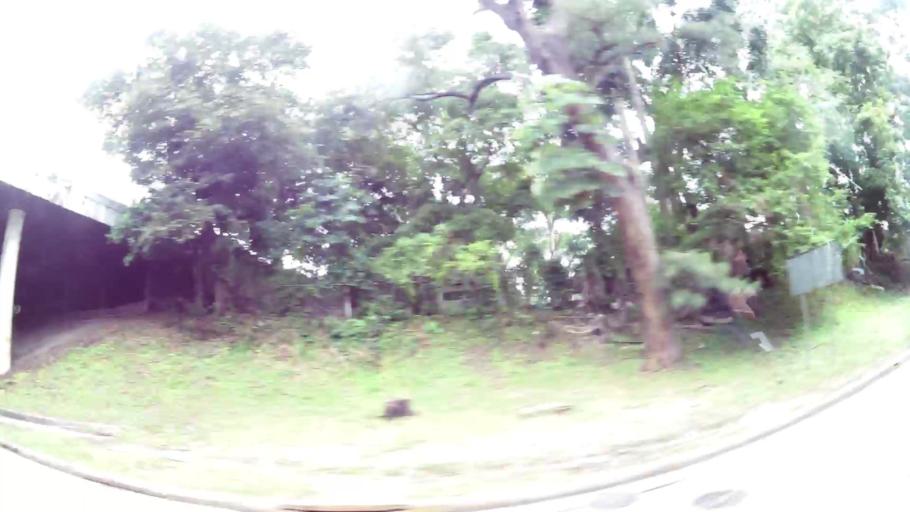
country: PA
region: Panama
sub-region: Distrito de Panama
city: Ancon
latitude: 8.9474
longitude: -79.5554
